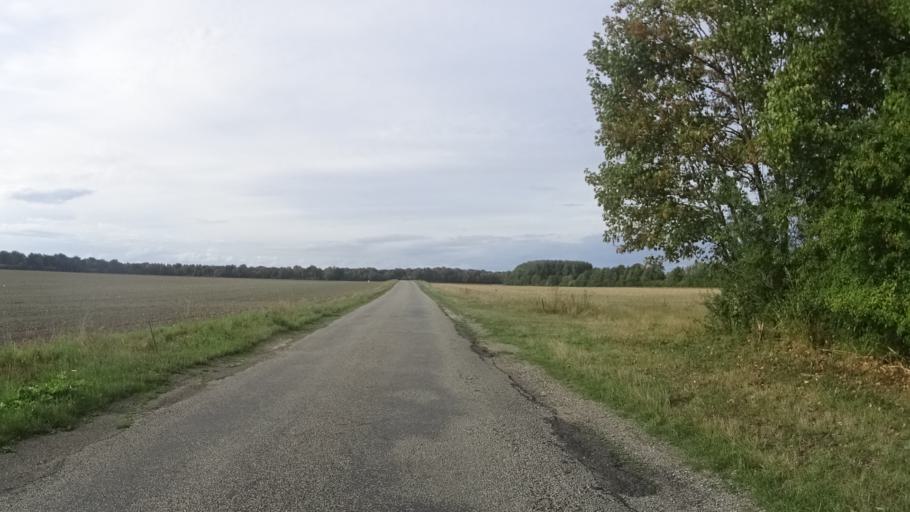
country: FR
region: Picardie
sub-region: Departement de l'Oise
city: Ver-sur-Launette
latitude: 49.1513
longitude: 2.6830
